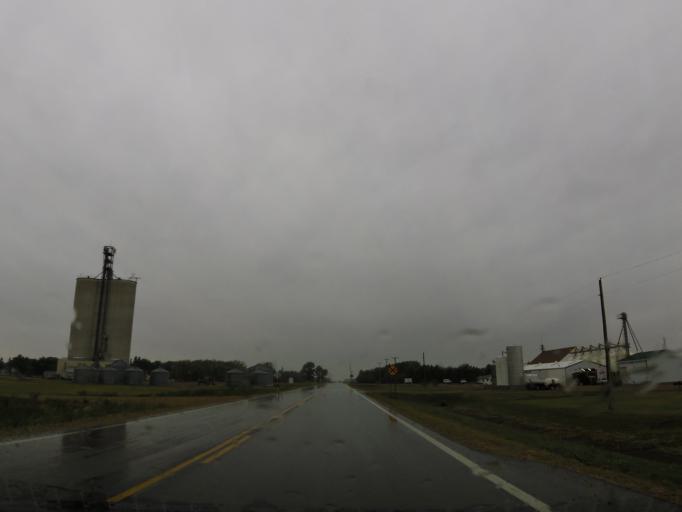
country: US
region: Minnesota
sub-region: Marshall County
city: Warren
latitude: 48.4561
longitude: -96.8720
